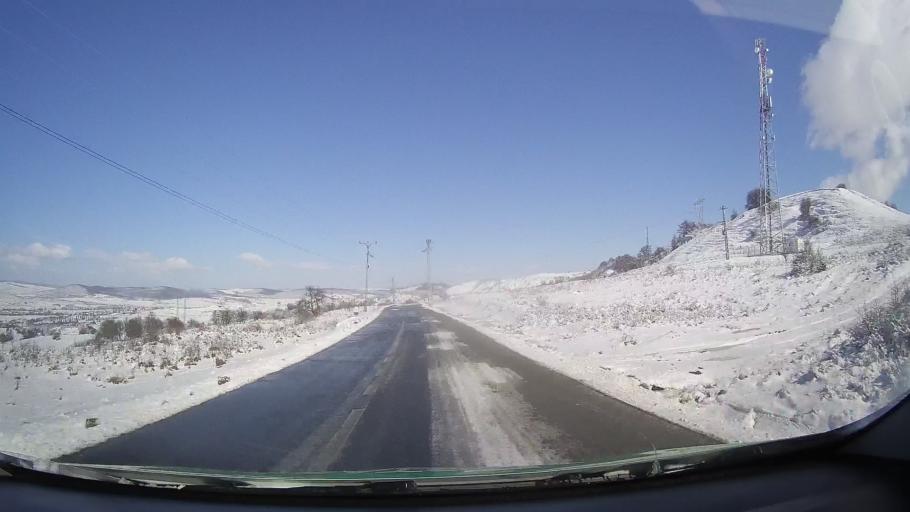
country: RO
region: Sibiu
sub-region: Comuna Avrig
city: Avrig
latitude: 45.7730
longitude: 24.3668
